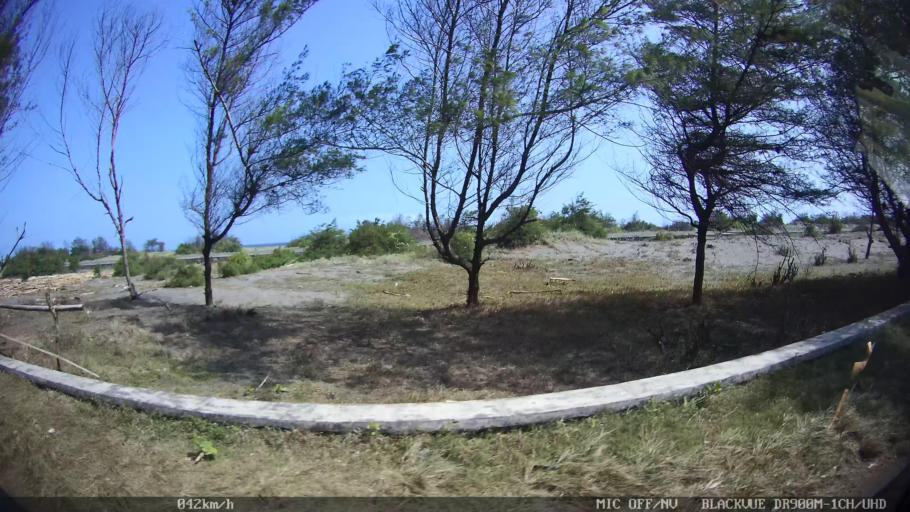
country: ID
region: Daerah Istimewa Yogyakarta
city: Bambanglipuro
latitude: -8.0154
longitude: 110.3014
